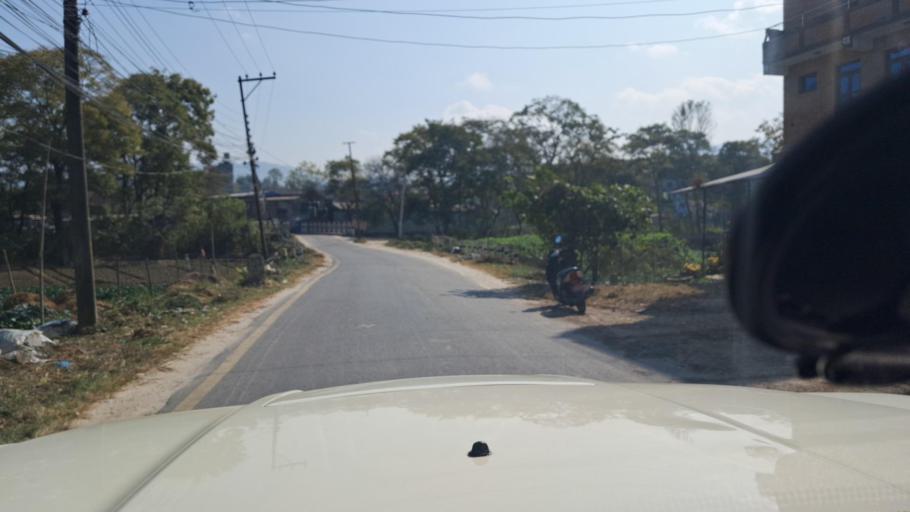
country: NP
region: Central Region
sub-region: Bagmati Zone
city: Bhaktapur
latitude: 27.6739
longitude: 85.4471
